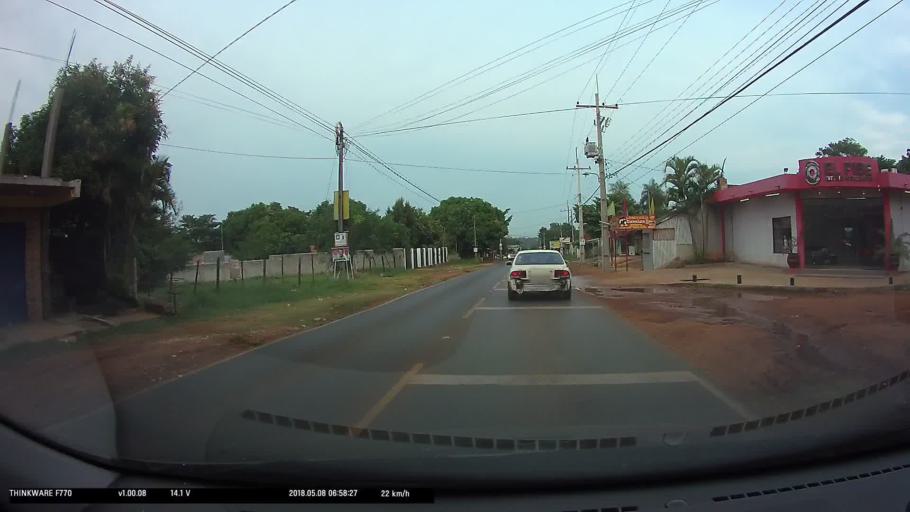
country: PY
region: Central
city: Limpio
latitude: -25.2453
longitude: -57.4816
